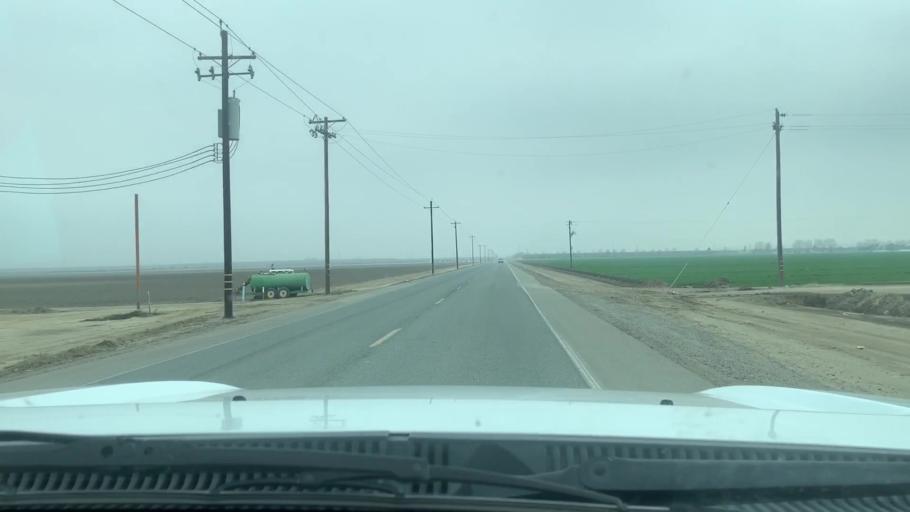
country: US
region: California
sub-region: Kern County
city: Buttonwillow
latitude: 35.5005
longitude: -119.4663
